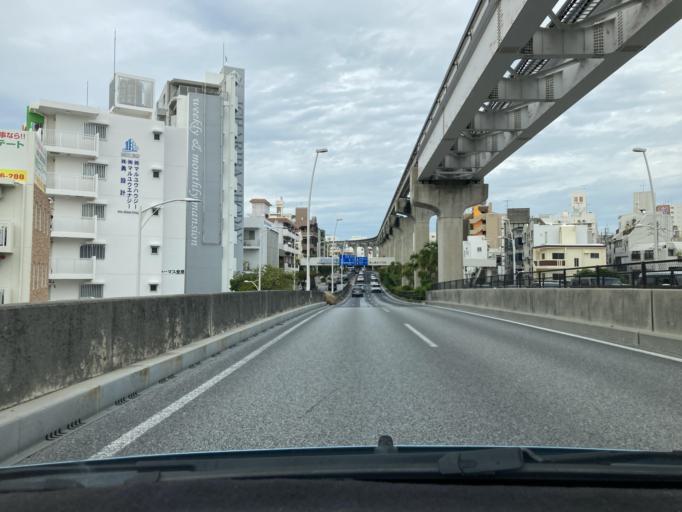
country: JP
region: Okinawa
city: Naha-shi
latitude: 26.2190
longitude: 127.6970
